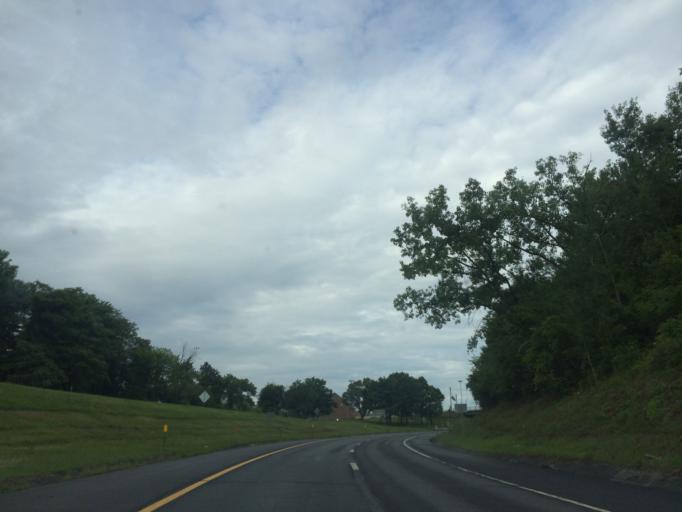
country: US
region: New York
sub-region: Albany County
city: Albany
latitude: 42.6332
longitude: -73.7726
